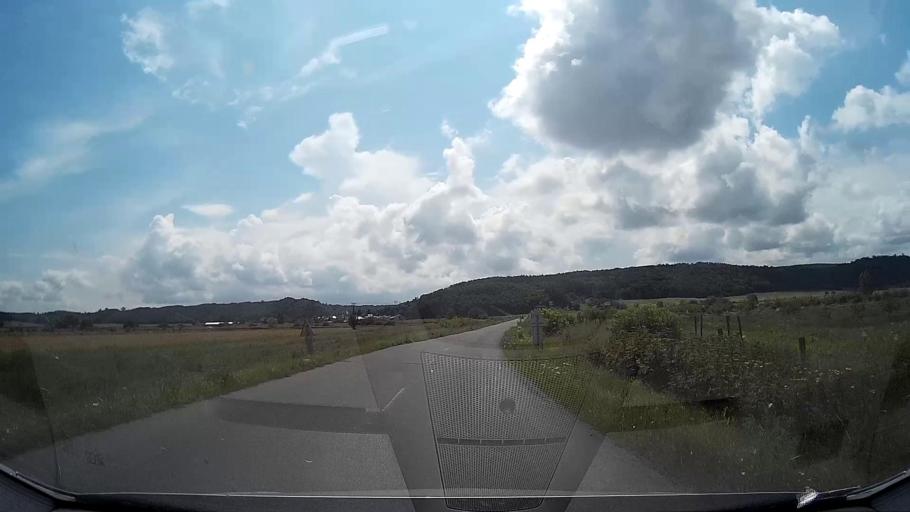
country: SK
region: Banskobystricky
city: Fil'akovo
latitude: 48.2940
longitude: 19.7901
